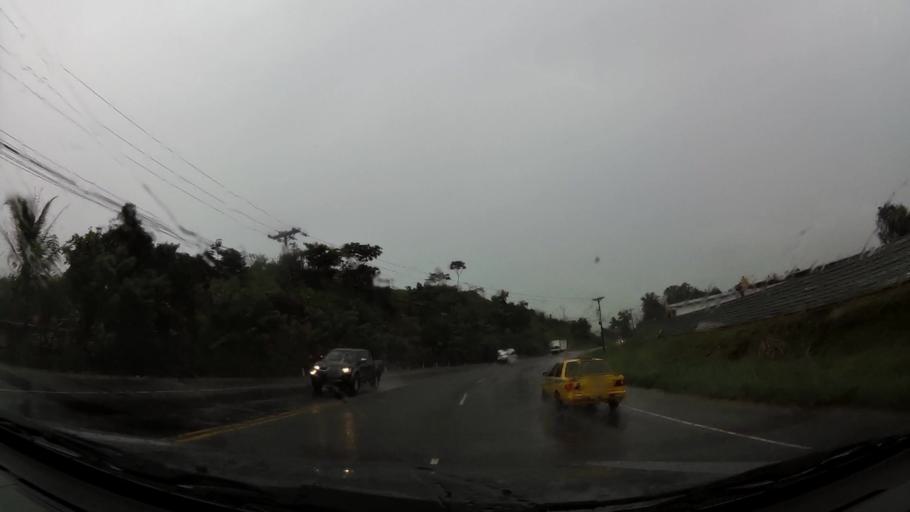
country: PA
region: Colon
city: Gatun
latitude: 9.2924
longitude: -79.7740
